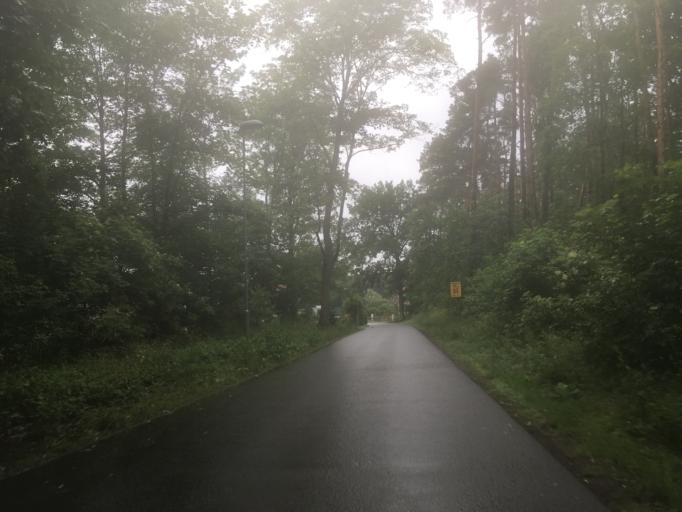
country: DE
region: Brandenburg
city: Liebenwalde
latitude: 52.8823
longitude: 13.3819
